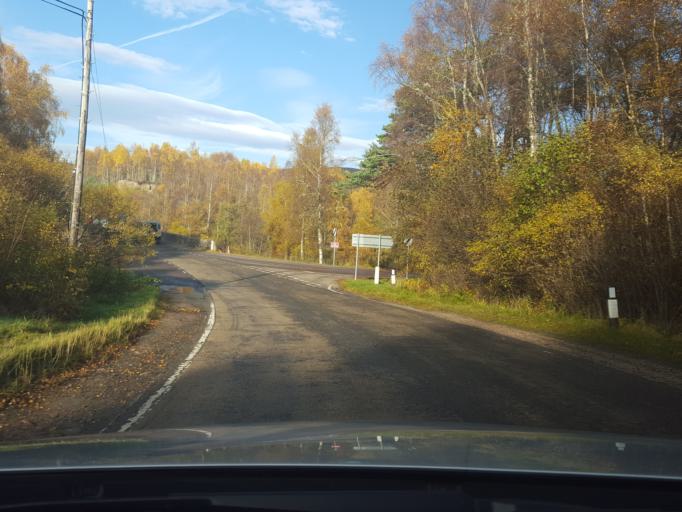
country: GB
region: Scotland
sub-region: Highland
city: Spean Bridge
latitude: 57.1752
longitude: -4.7980
